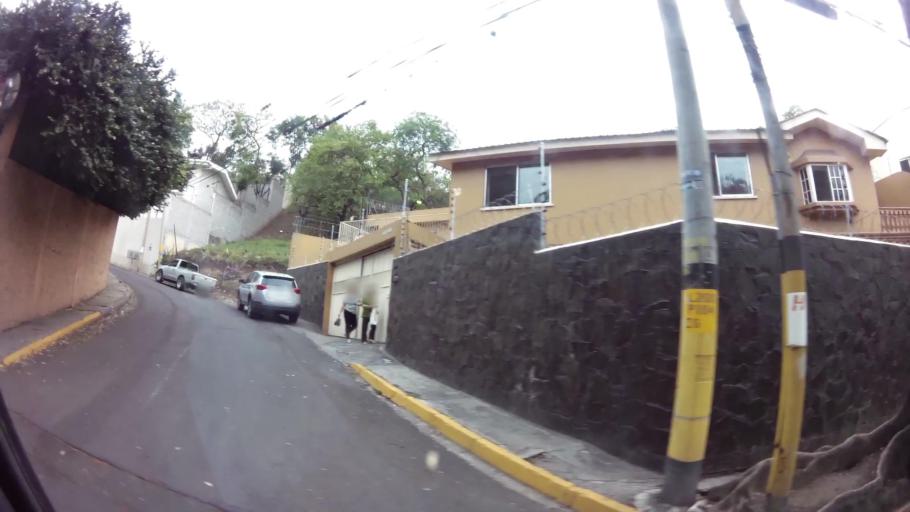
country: HN
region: Francisco Morazan
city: Tegucigalpa
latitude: 14.0954
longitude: -87.1809
